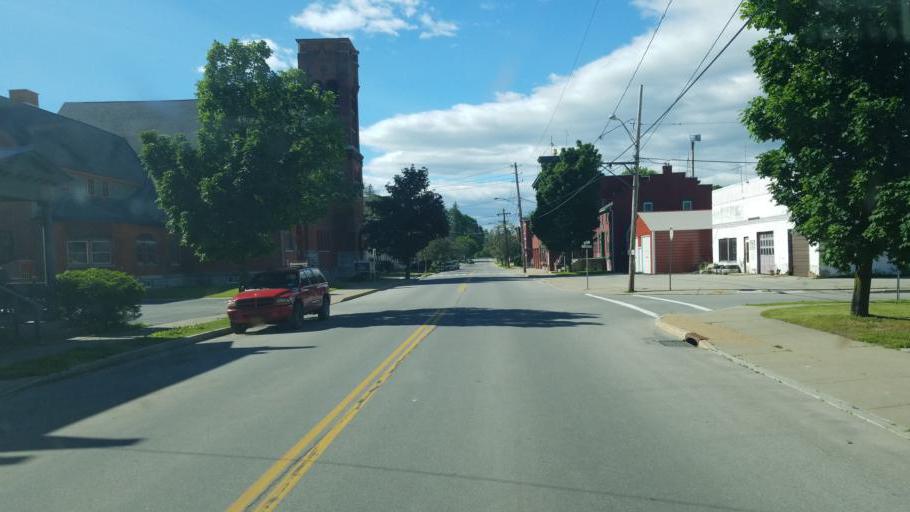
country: US
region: New York
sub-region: Montgomery County
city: Fort Plain
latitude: 42.9328
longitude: -74.6241
